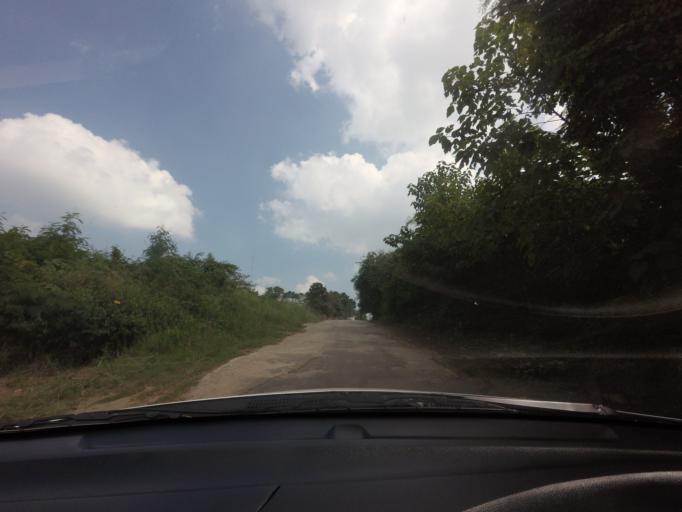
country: TH
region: Nakhon Ratchasima
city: Pak Chong
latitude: 14.5430
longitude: 101.5945
